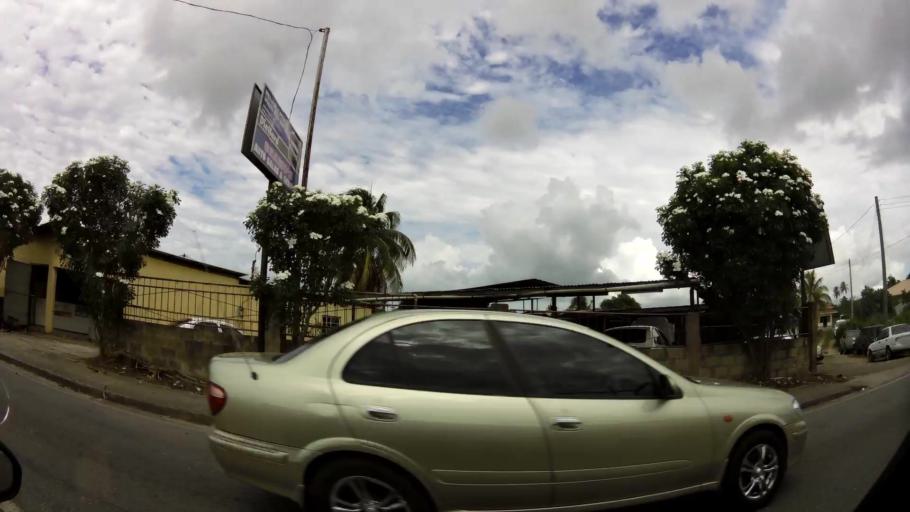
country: TT
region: Couva-Tabaquite-Talparo
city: Couva
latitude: 10.4441
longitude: -61.4494
